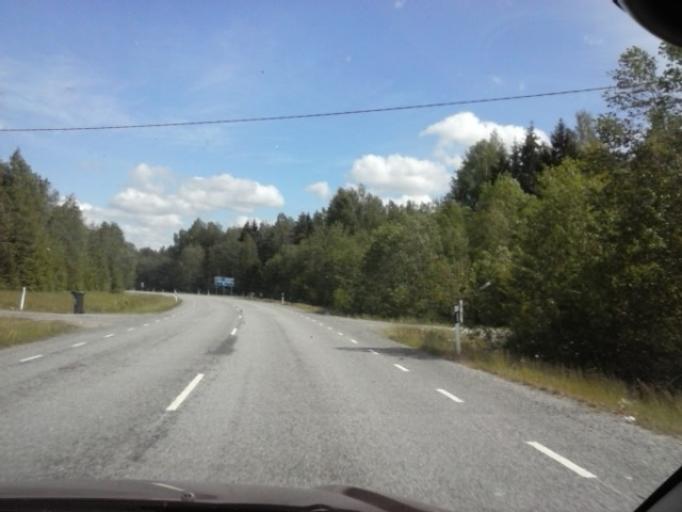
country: EE
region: Raplamaa
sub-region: Rapla vald
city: Rapla
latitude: 58.9906
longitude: 24.7779
